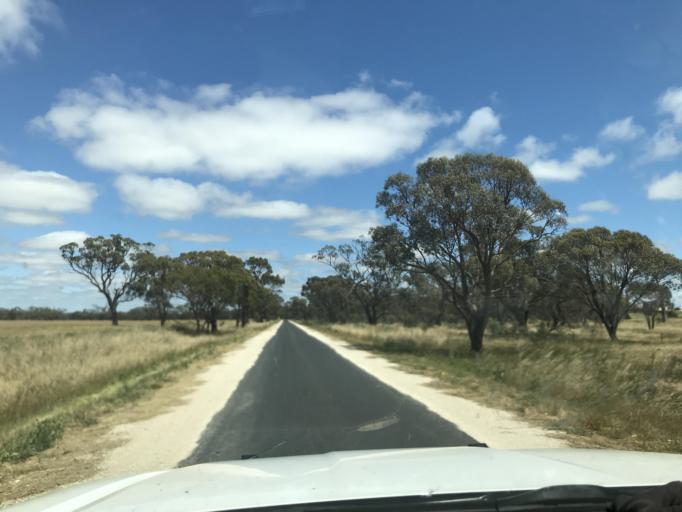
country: AU
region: South Australia
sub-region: Tatiara
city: Bordertown
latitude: -36.3086
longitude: 141.0478
